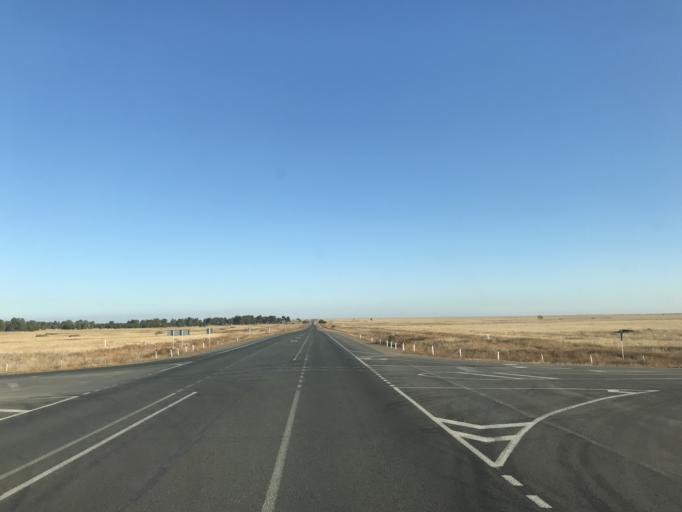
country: KZ
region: Pavlodar
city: Kurchatov
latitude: 51.1870
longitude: 78.6995
